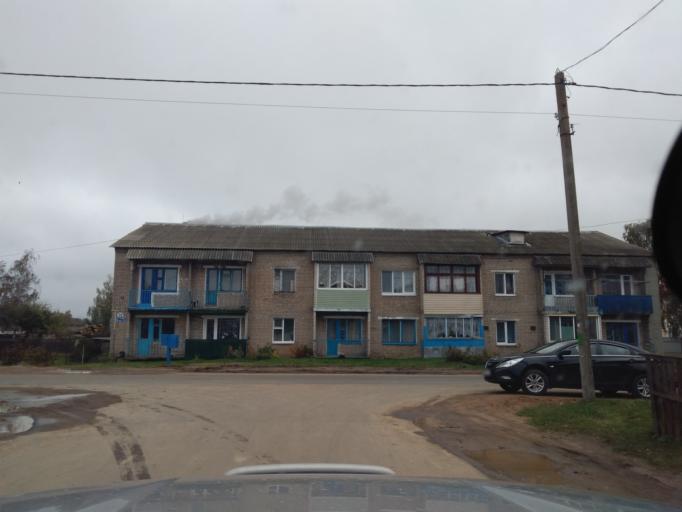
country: BY
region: Minsk
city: Kapyl'
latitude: 53.1407
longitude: 27.0922
